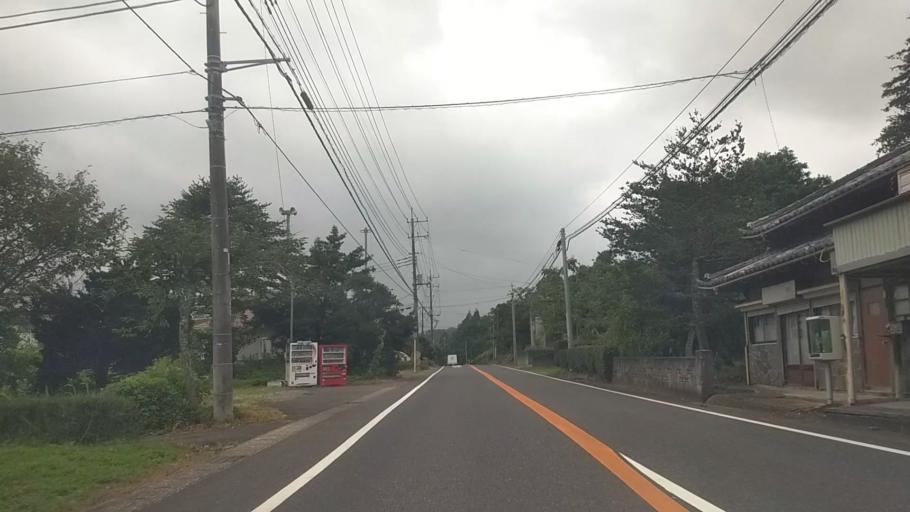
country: JP
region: Chiba
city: Kawaguchi
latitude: 35.2270
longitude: 140.0746
